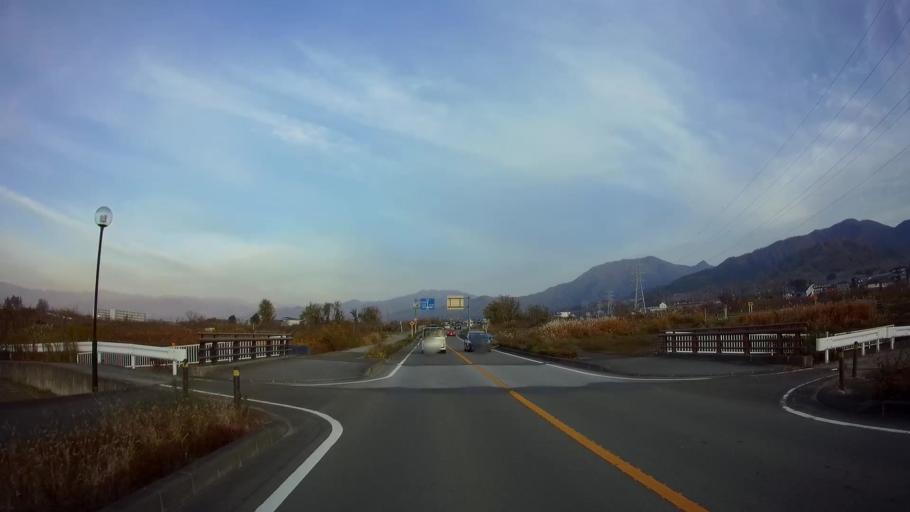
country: JP
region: Yamanashi
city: Isawa
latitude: 35.6076
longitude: 138.6221
